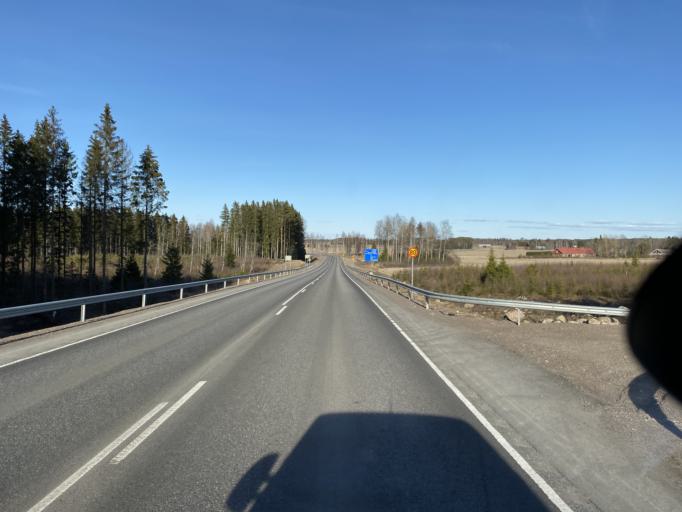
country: FI
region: Satakunta
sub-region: Pori
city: Huittinen
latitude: 61.1760
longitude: 22.5722
